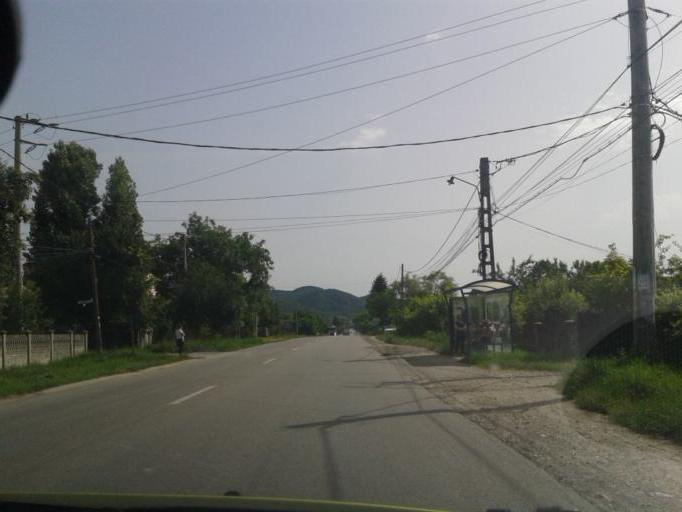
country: RO
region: Valcea
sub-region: Municipiul Ramnicu Valcea
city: Copacelu
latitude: 45.0615
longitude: 24.2995
